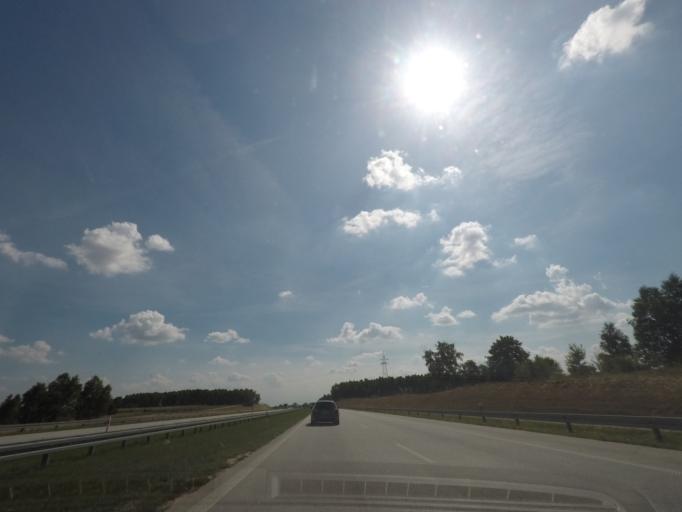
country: PL
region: Lodz Voivodeship
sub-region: Powiat lodzki wschodni
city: Andrespol
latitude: 51.7719
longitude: 19.6006
